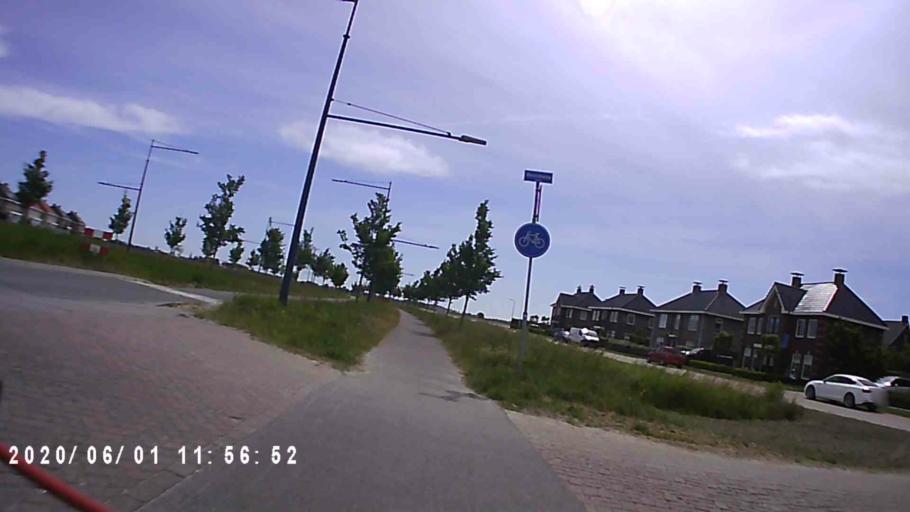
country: NL
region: Friesland
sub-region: Gemeente Harlingen
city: Harlingen
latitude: 53.1597
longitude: 5.4381
